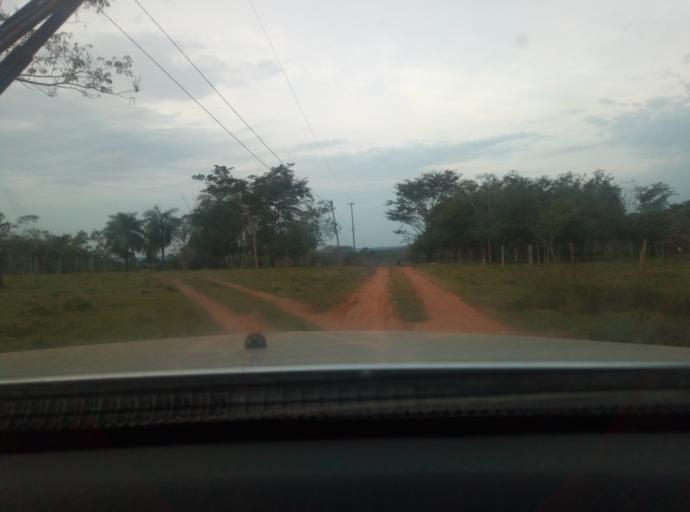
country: PY
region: Caaguazu
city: Carayao
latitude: -25.1479
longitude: -56.3838
